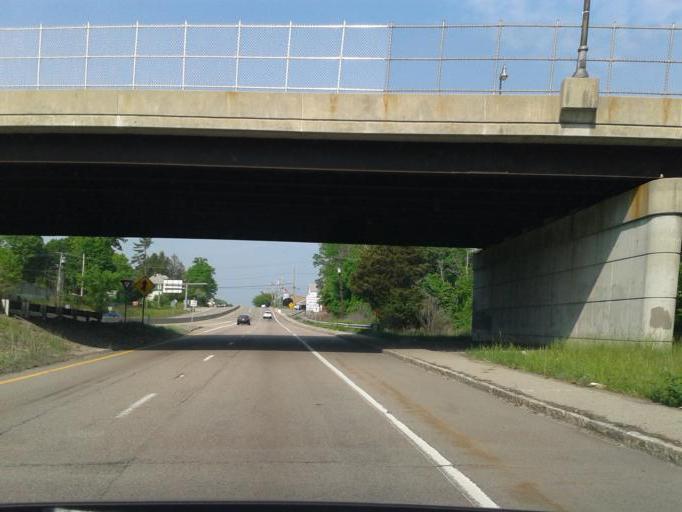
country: US
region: Massachusetts
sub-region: Worcester County
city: Southborough
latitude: 42.2975
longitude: -71.4906
